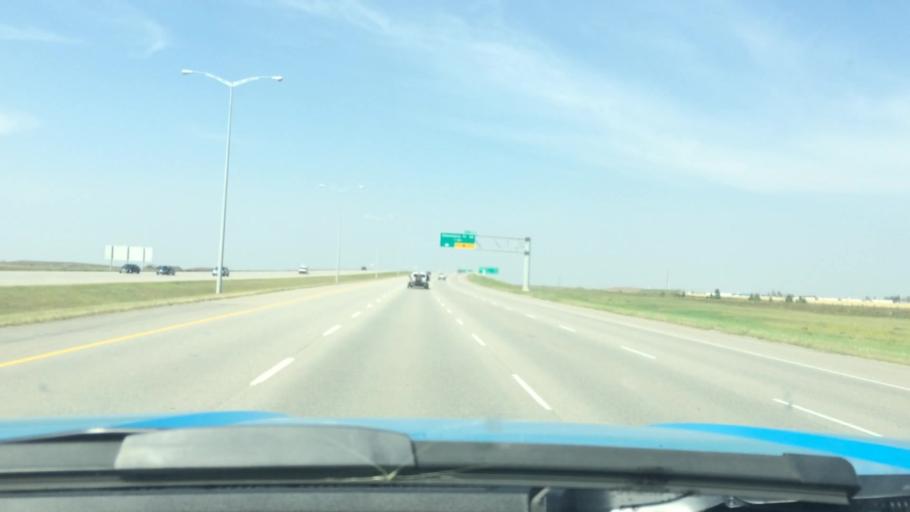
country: CA
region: Alberta
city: Chestermere
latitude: 50.9644
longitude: -113.9207
